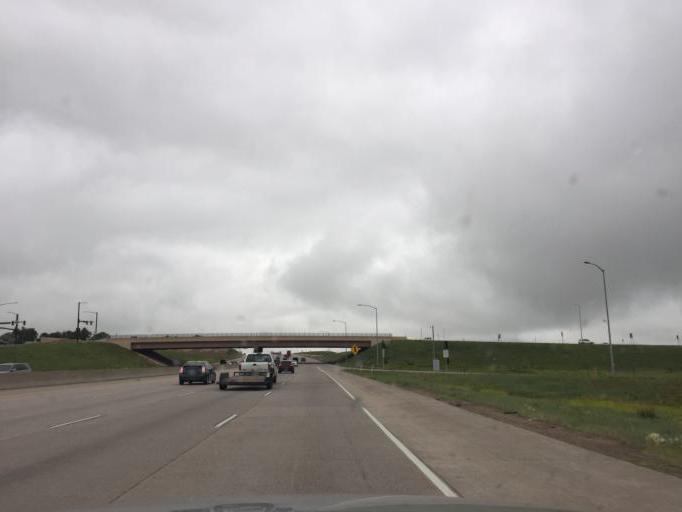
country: US
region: Colorado
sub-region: Park County
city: Castle Pines North
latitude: 39.4701
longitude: -104.8727
